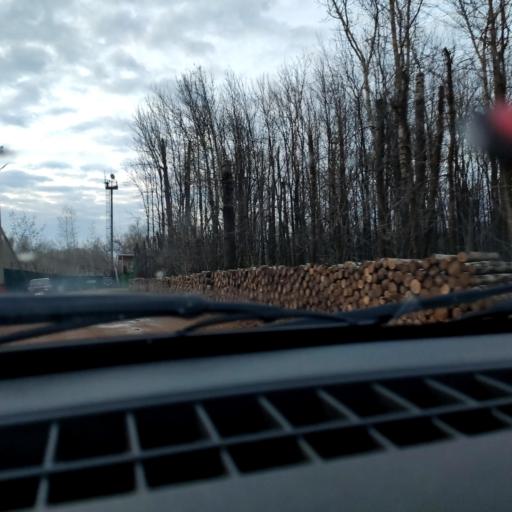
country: RU
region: Bashkortostan
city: Ufa
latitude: 54.6737
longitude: 55.9505
